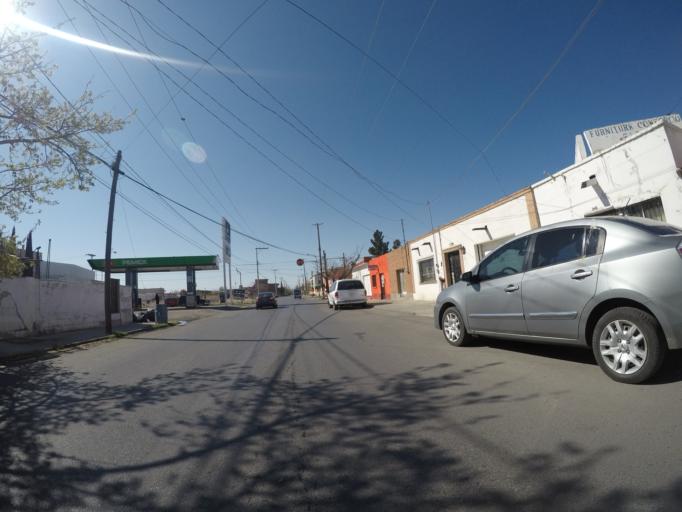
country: MX
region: Chihuahua
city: Ciudad Juarez
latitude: 31.7445
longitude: -106.4734
